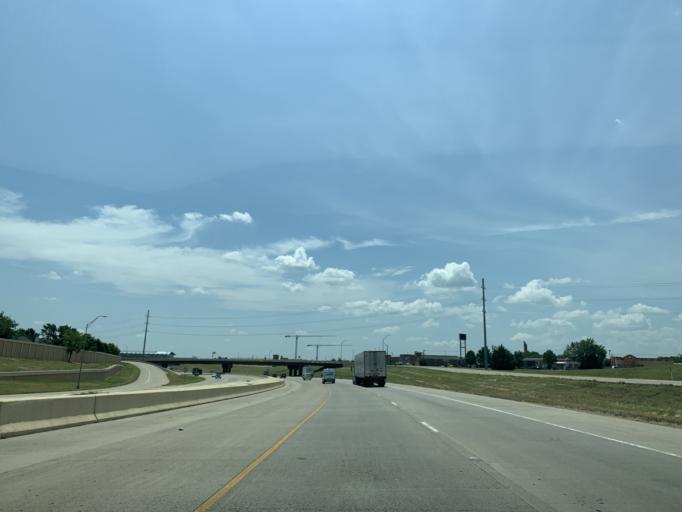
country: US
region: Texas
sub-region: Denton County
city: Roanoke
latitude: 33.0036
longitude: -97.2182
